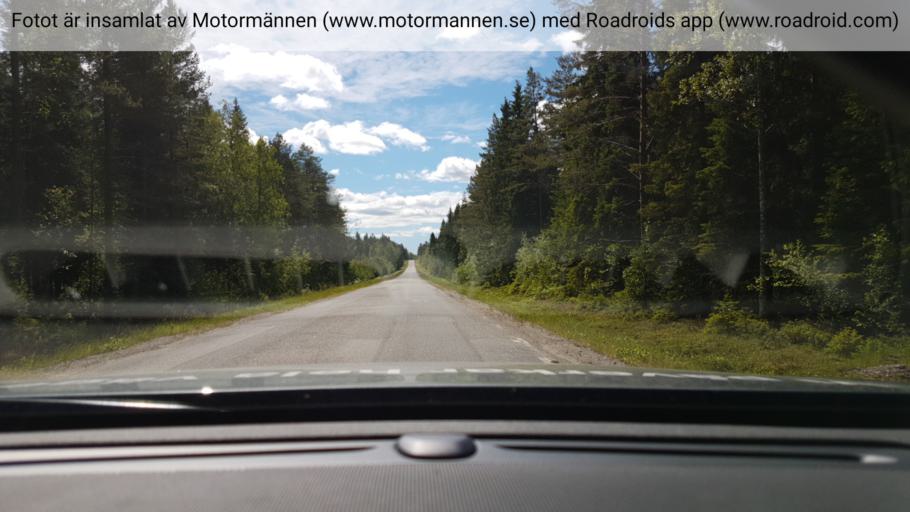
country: SE
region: Vaesterbotten
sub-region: Skelleftea Kommun
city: Burea
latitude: 64.4313
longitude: 21.3537
